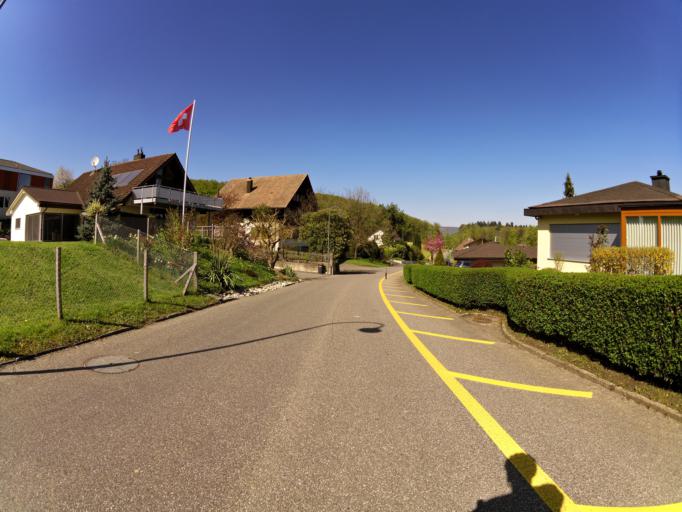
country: CH
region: Solothurn
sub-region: Bezirk Olten
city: Schonenwerd
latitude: 47.3763
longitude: 8.0251
